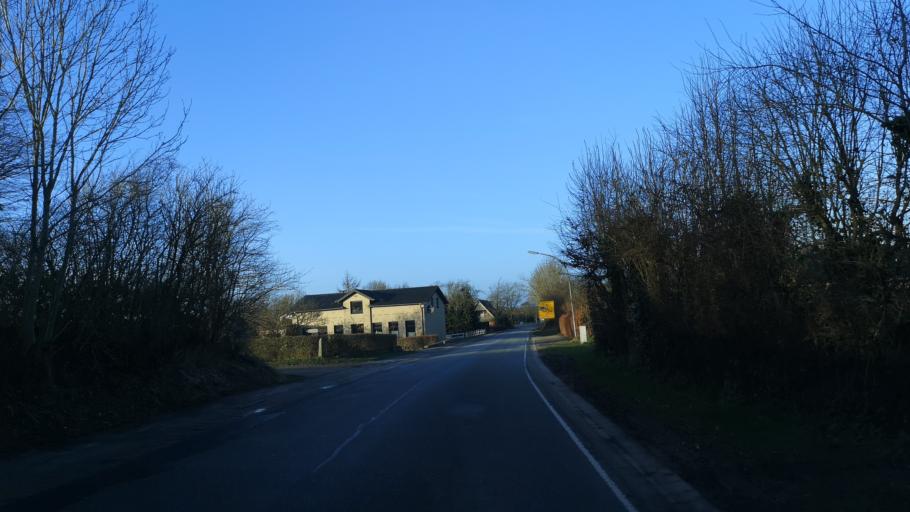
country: DE
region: Schleswig-Holstein
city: Grosssolt
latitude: 54.7032
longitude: 9.5325
